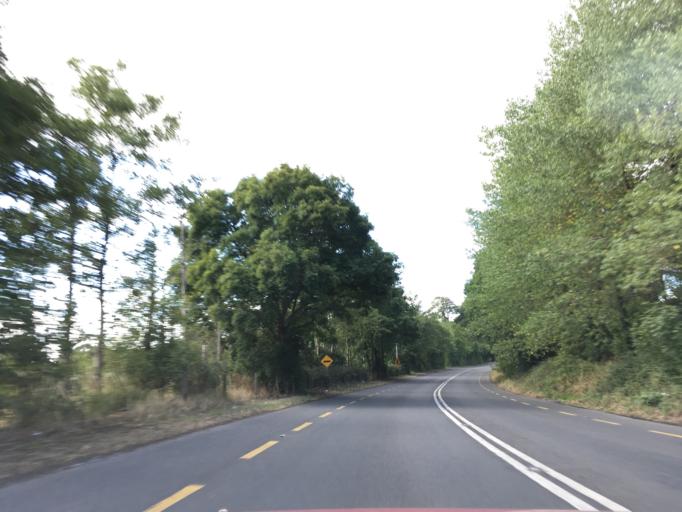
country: IE
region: Munster
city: Cahir
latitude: 52.4177
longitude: -7.8886
